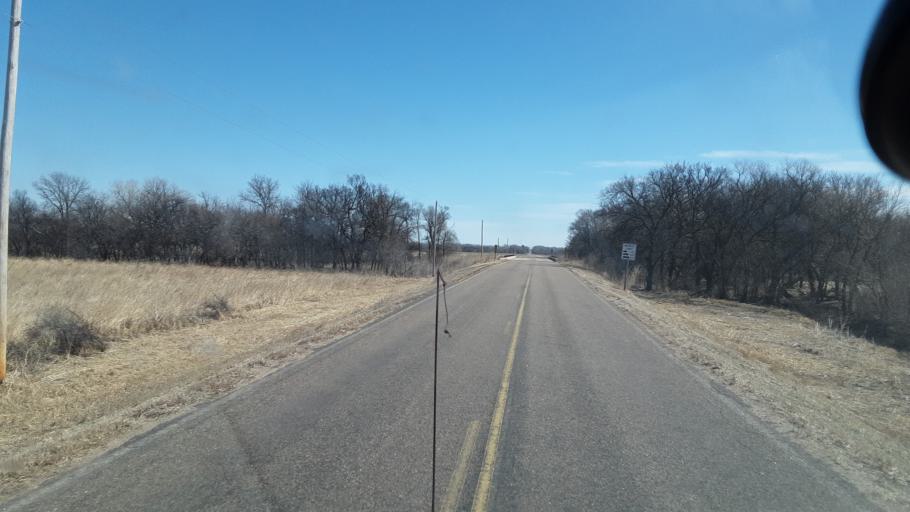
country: US
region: Kansas
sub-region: Reno County
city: Nickerson
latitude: 38.2174
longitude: -98.0618
